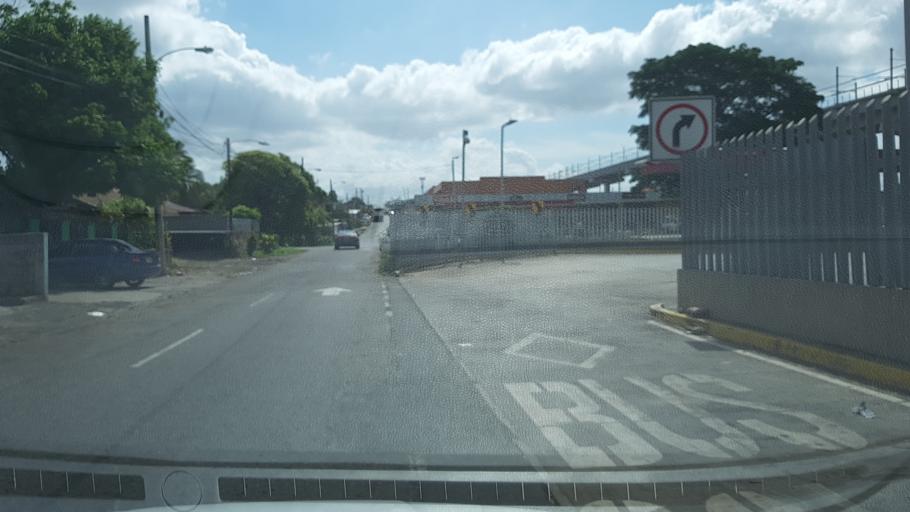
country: PA
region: Panama
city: San Miguelito
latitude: 9.0606
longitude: -79.4290
